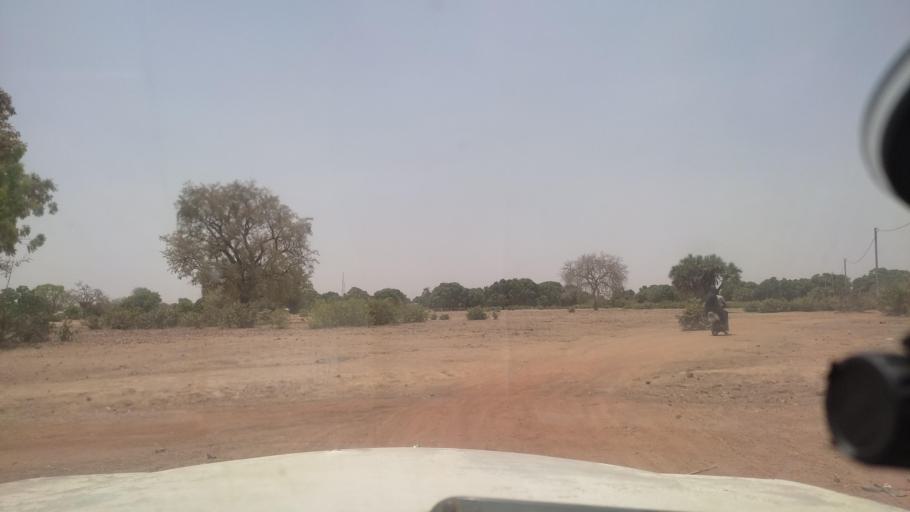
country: BF
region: Est
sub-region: Province du Gourma
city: Fada N'gourma
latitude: 12.0743
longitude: 0.3799
